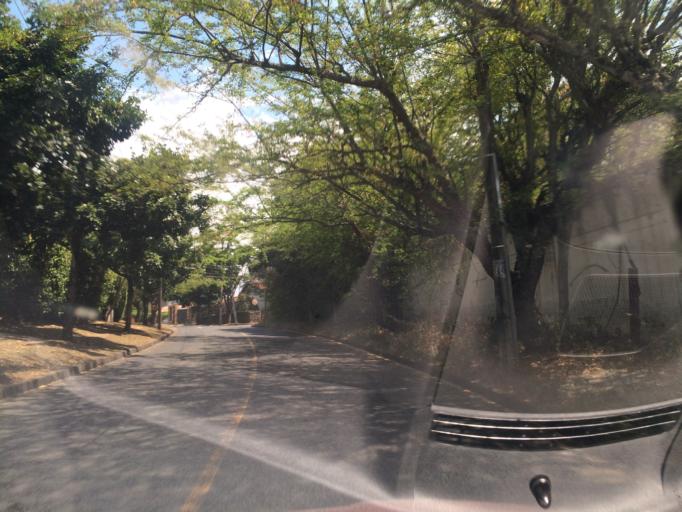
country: CO
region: Valle del Cauca
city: Cali
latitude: 3.3577
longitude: -76.5417
